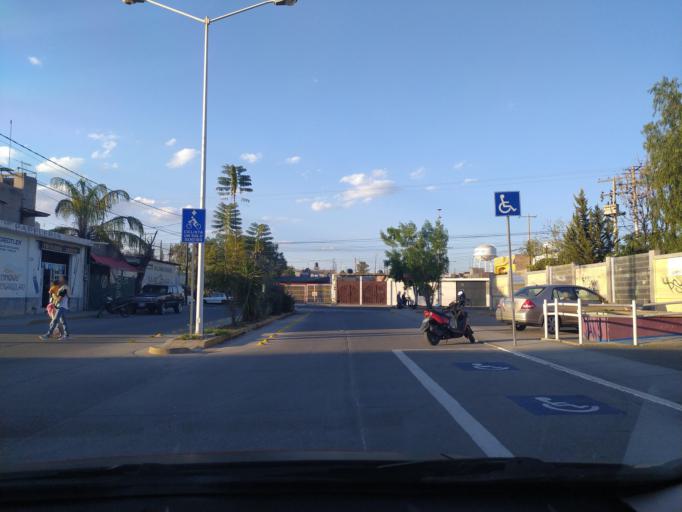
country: MX
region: Guanajuato
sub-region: San Francisco del Rincon
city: Fraccionamiento la Mezquitera
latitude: 21.0121
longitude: -101.8408
